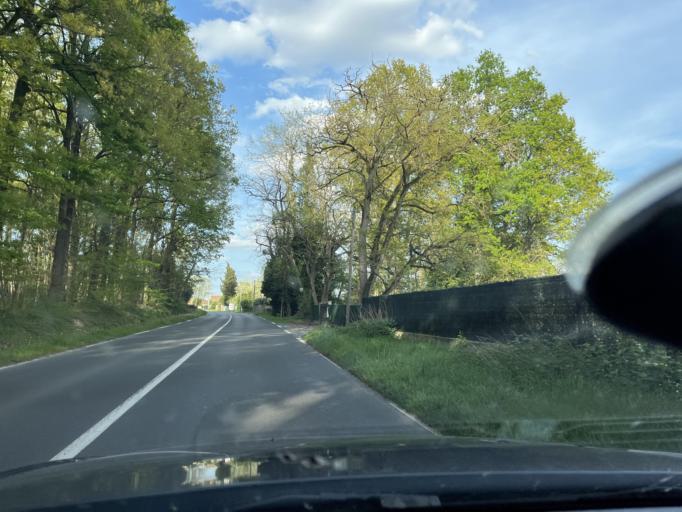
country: FR
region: Ile-de-France
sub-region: Departement de l'Essonne
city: Breuillet
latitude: 48.5588
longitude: 2.1507
